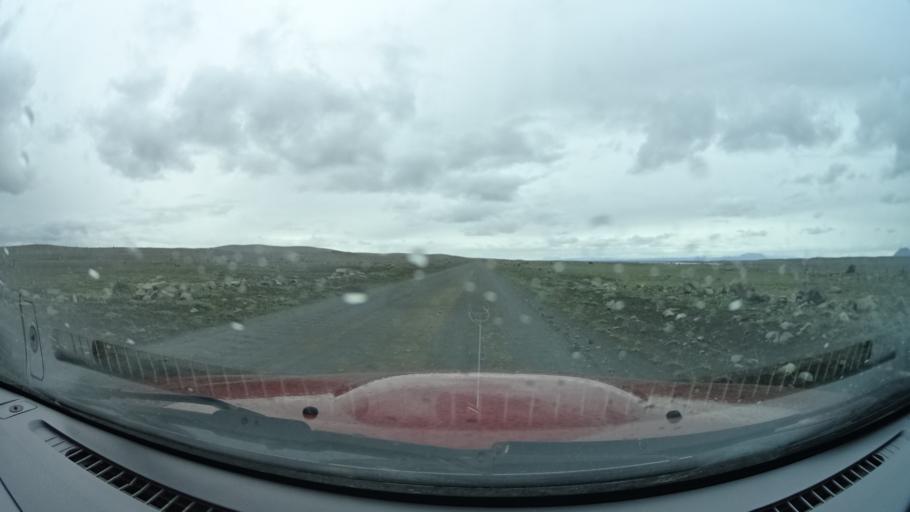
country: IS
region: Northeast
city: Husavik
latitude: 65.7786
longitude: -16.3485
